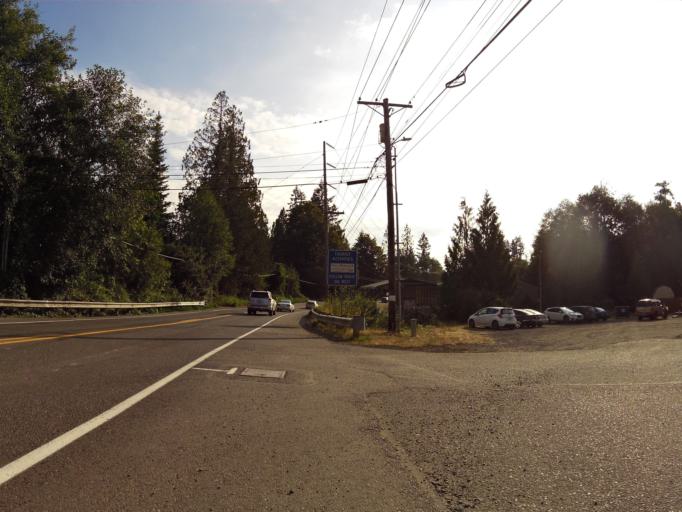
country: US
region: Washington
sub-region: Mason County
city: Belfair
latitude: 47.4377
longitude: -122.8360
